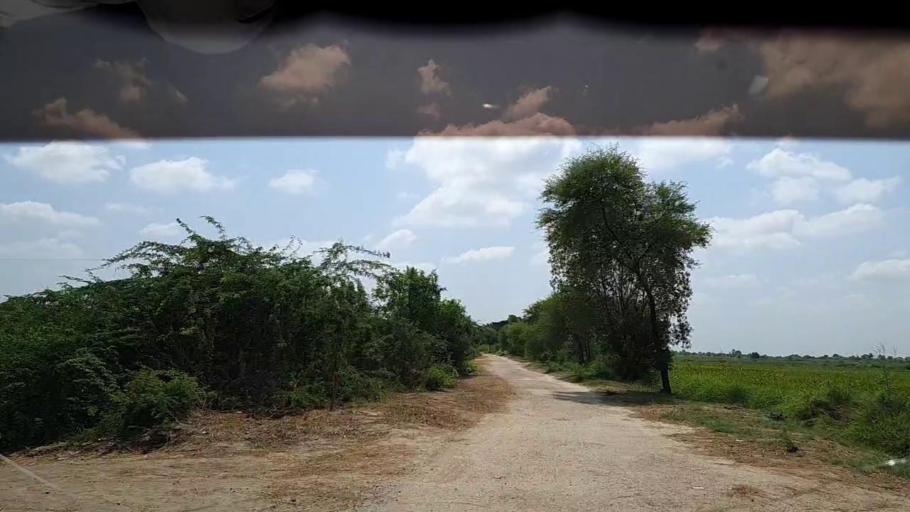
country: PK
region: Sindh
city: Kadhan
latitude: 24.5928
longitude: 68.9582
